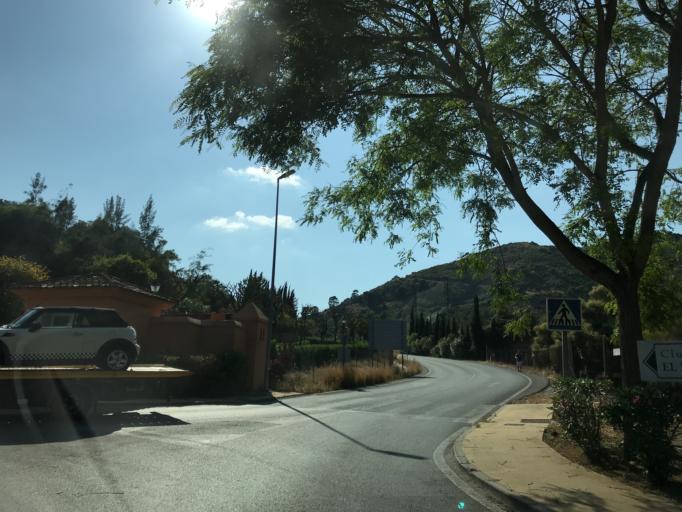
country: ES
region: Andalusia
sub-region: Provincia de Malaga
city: Benahavis
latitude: 36.5073
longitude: -5.0157
